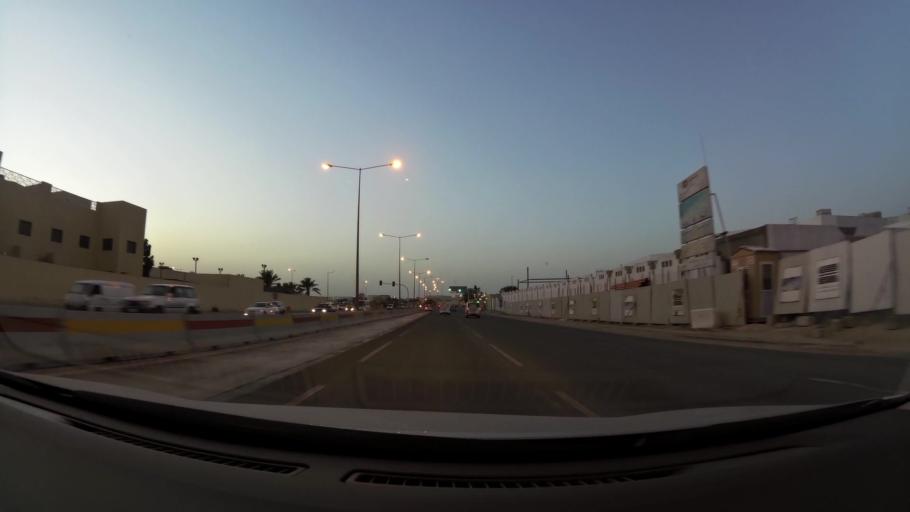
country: QA
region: Baladiyat ar Rayyan
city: Ar Rayyan
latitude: 25.3093
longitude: 51.4626
